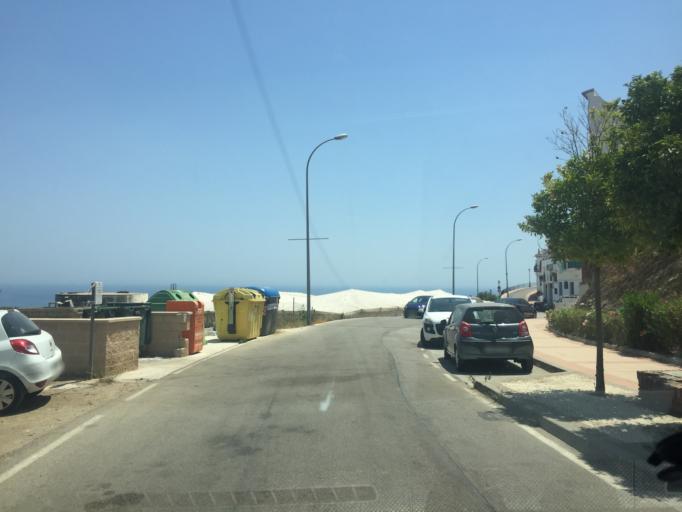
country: ES
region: Andalusia
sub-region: Provincia de Malaga
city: Nerja
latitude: 36.7588
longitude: -3.8421
